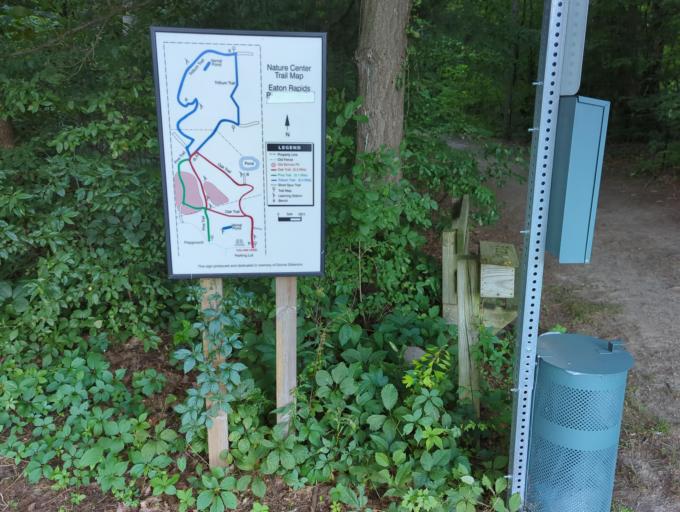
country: US
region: Michigan
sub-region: Eaton County
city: Eaton Rapids
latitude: 42.5197
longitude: -84.6631
